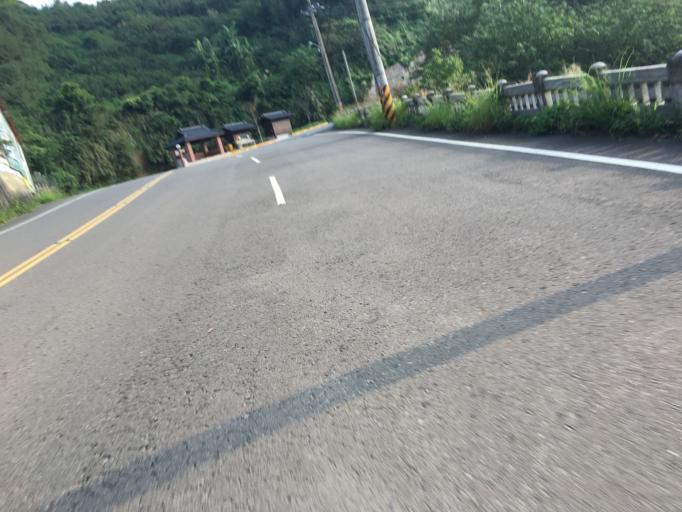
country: TW
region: Taiwan
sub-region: Hsinchu
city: Hsinchu
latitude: 24.7273
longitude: 121.0346
